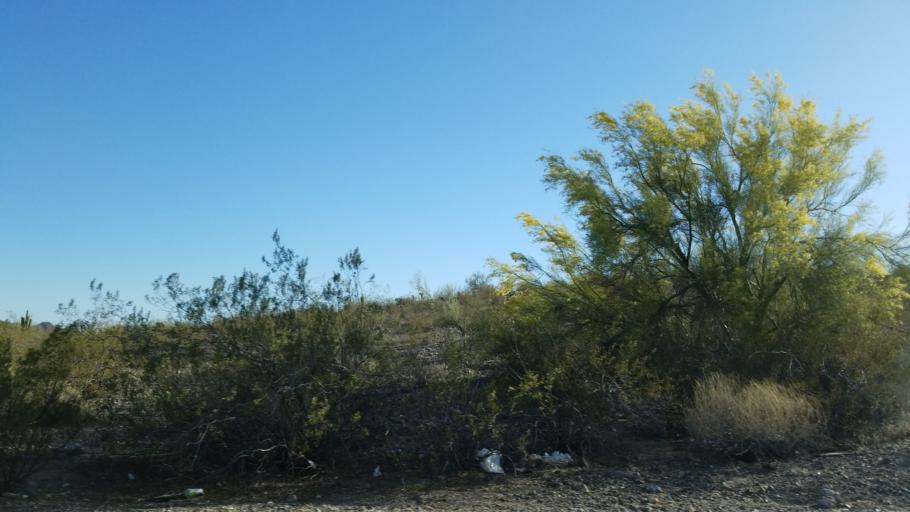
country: US
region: Arizona
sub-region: Maricopa County
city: Paradise Valley
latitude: 33.5988
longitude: -112.0453
